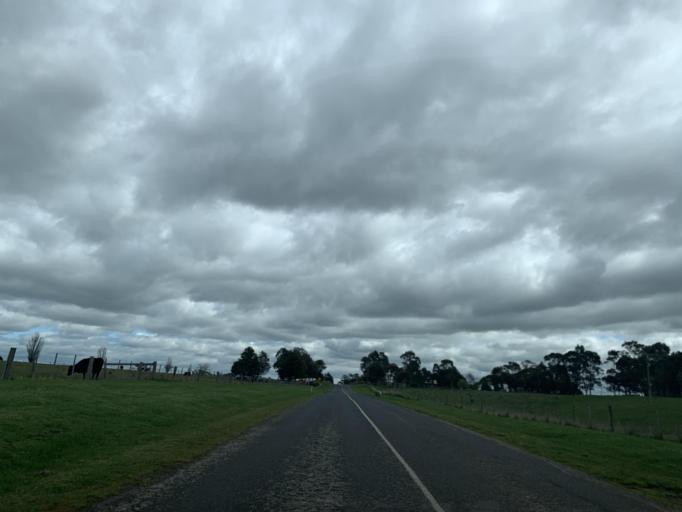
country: AU
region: Victoria
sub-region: Whittlesea
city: Whittlesea
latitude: -37.1859
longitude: 145.0281
